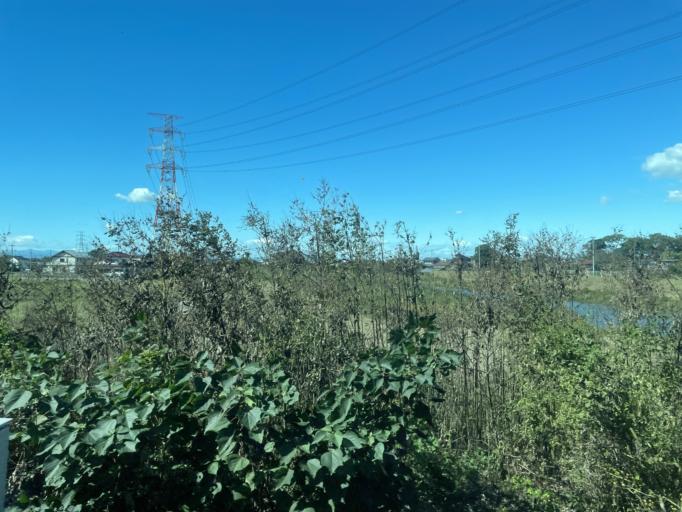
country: JP
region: Saitama
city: Kurihashi
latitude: 36.1089
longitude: 139.6791
